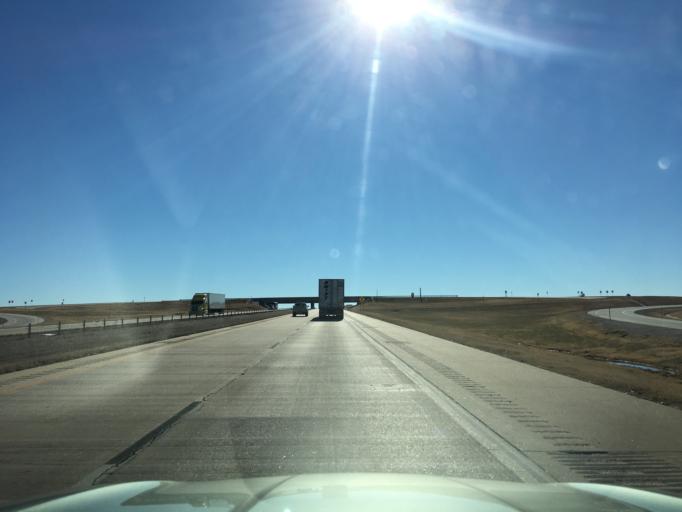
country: US
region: Oklahoma
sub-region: Noble County
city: Perry
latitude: 36.4039
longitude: -97.3272
